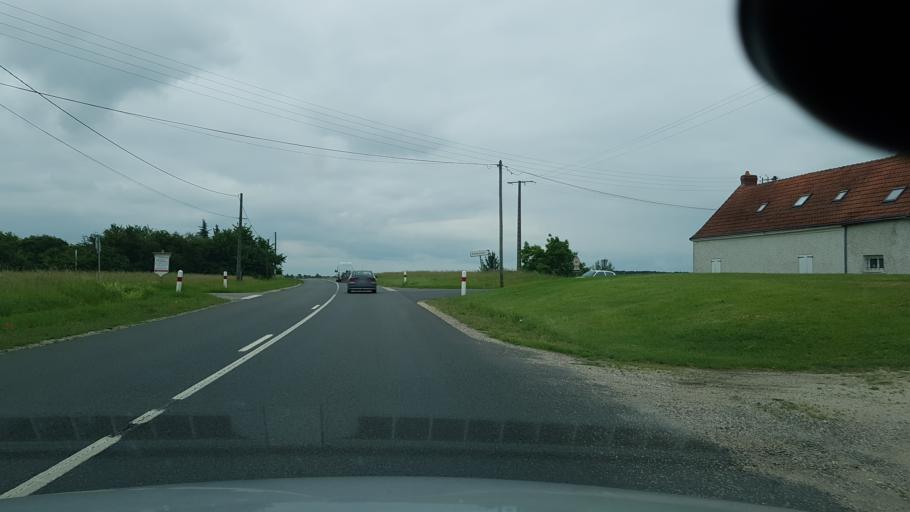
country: FR
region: Centre
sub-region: Departement du Loir-et-Cher
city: Chatillon-sur-Cher
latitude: 47.3023
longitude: 1.5103
